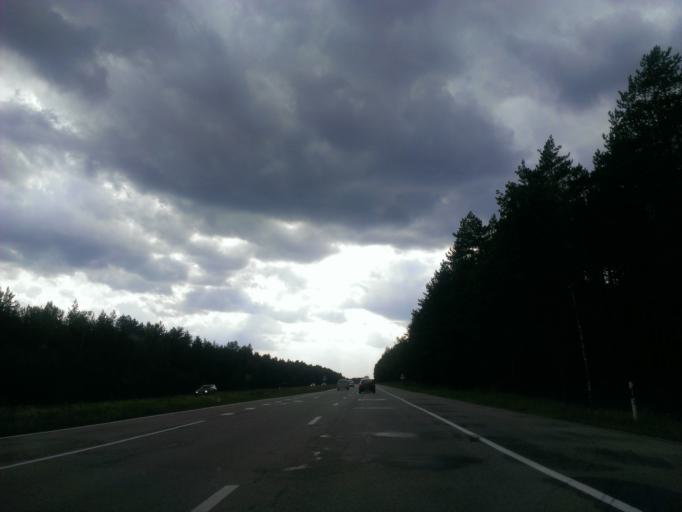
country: LV
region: Krimulda
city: Ragana
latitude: 57.1316
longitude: 24.7436
